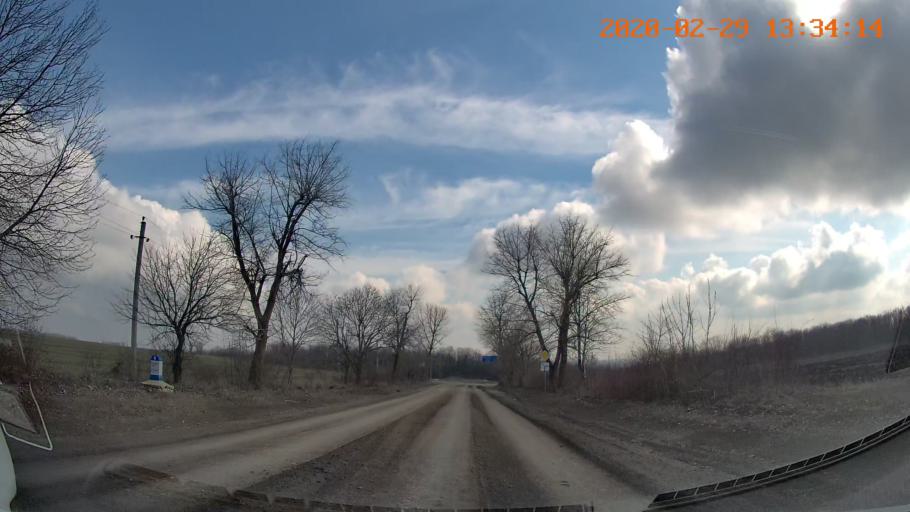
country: MD
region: Telenesti
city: Camenca
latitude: 47.8699
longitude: 28.6214
